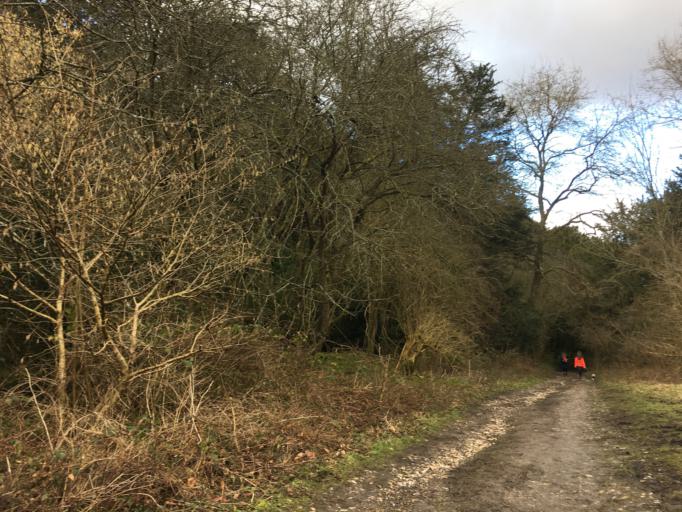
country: GB
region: England
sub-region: Surrey
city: Mickleham
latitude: 51.2545
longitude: -0.3073
